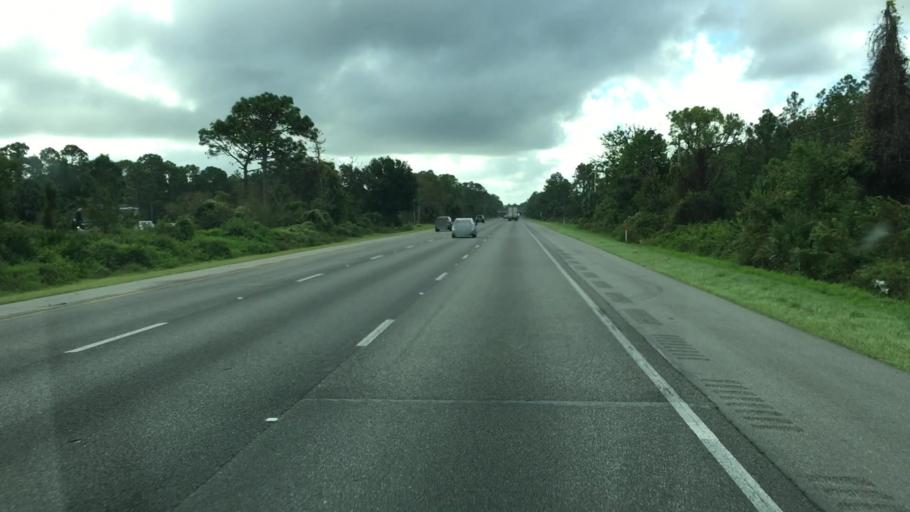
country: US
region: Florida
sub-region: Volusia County
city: Glencoe
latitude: 29.0575
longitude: -81.0082
